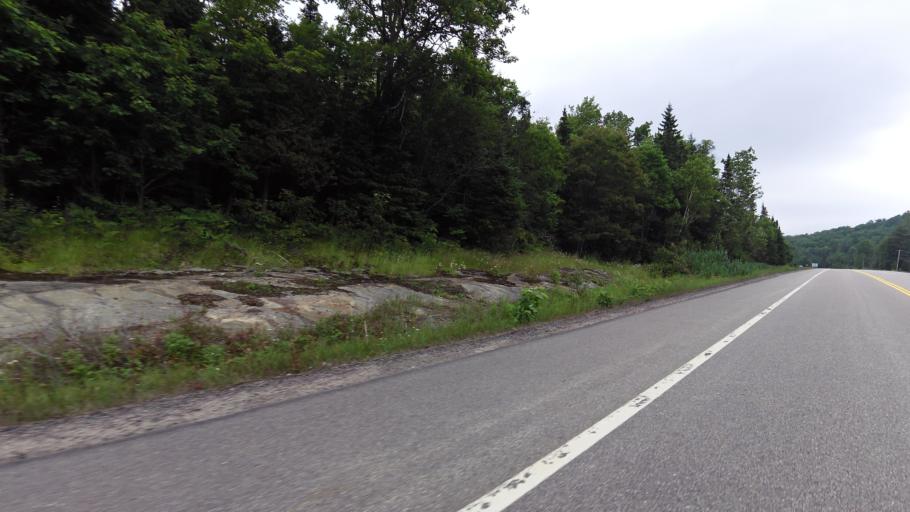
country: CA
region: Ontario
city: Huntsville
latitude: 45.3307
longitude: -78.9591
